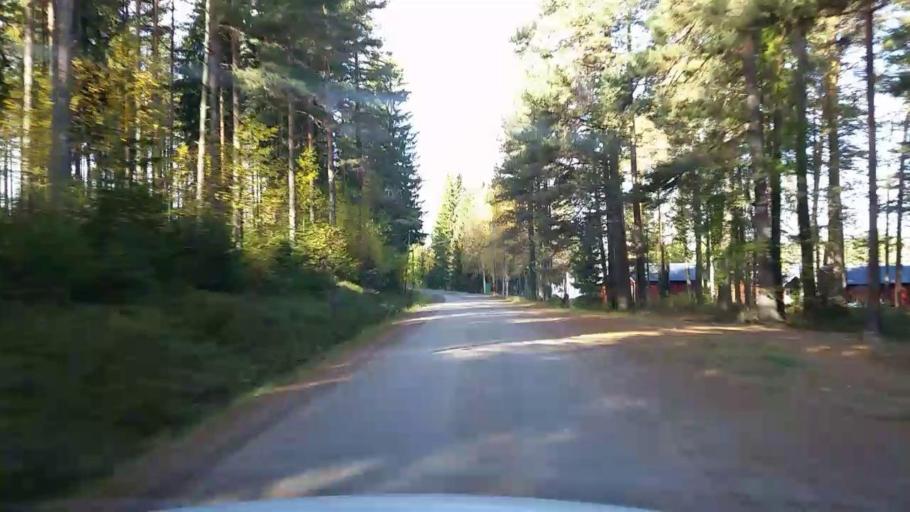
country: SE
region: Gaevleborg
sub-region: Ljusdals Kommun
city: Jaervsoe
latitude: 61.7900
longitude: 16.1851
